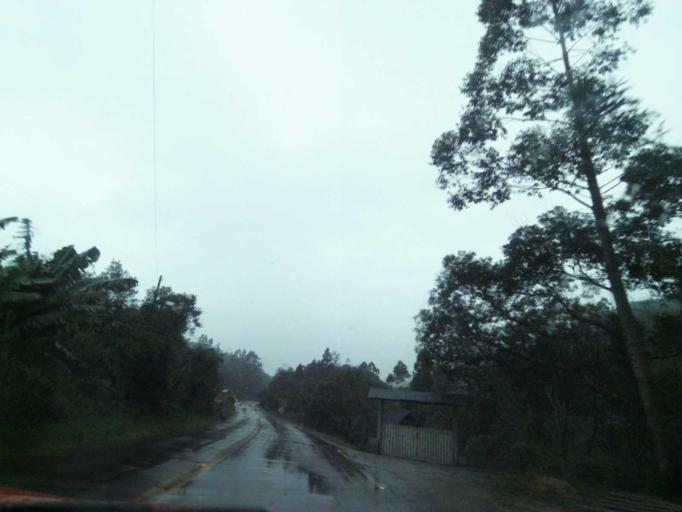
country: BR
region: Santa Catarina
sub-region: Anitapolis
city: Anitapolis
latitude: -27.8206
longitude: -49.0491
